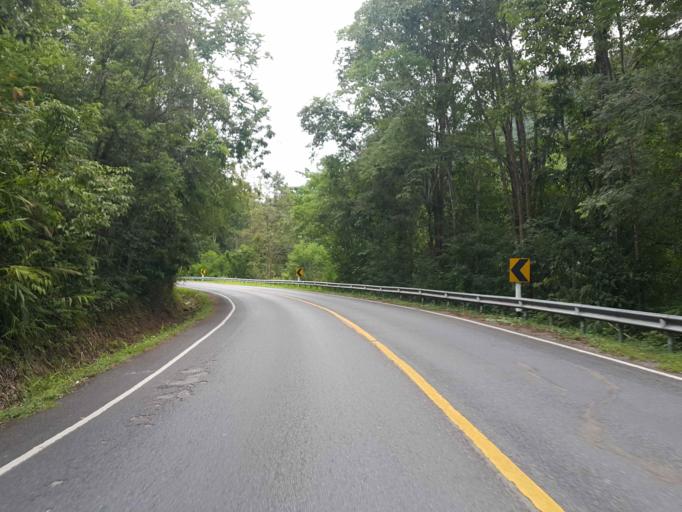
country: TH
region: Chiang Mai
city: Chom Thong
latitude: 18.5285
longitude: 98.6188
